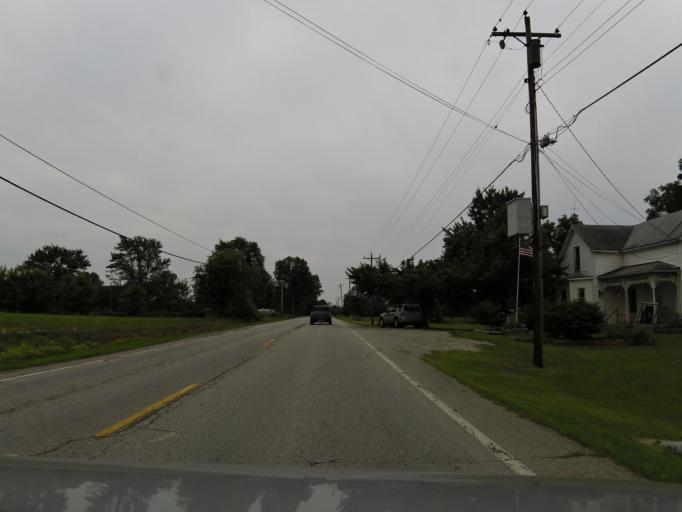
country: US
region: Ohio
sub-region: Brown County
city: Mount Orab
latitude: 39.0651
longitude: -83.9250
